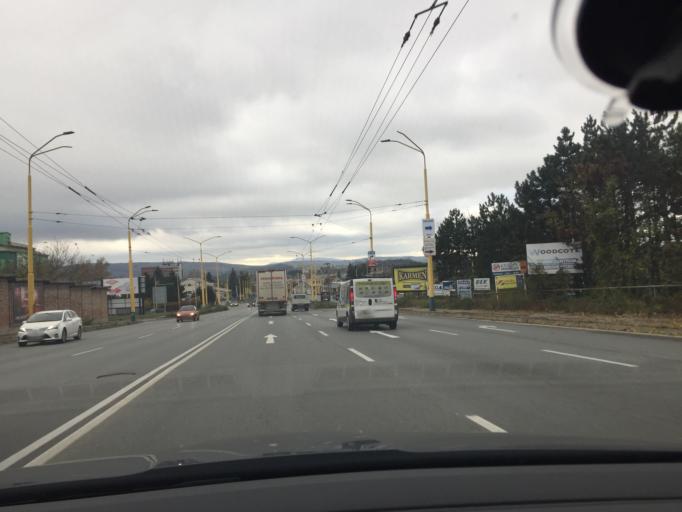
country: SK
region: Presovsky
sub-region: Okres Presov
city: Presov
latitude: 49.0137
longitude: 21.2652
